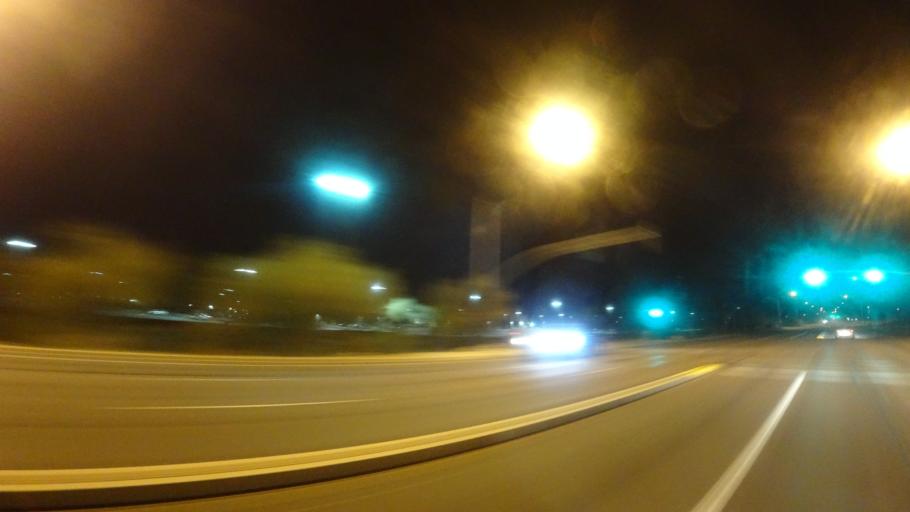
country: US
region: Arizona
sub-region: Maricopa County
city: Mesa
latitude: 33.4703
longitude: -111.7185
